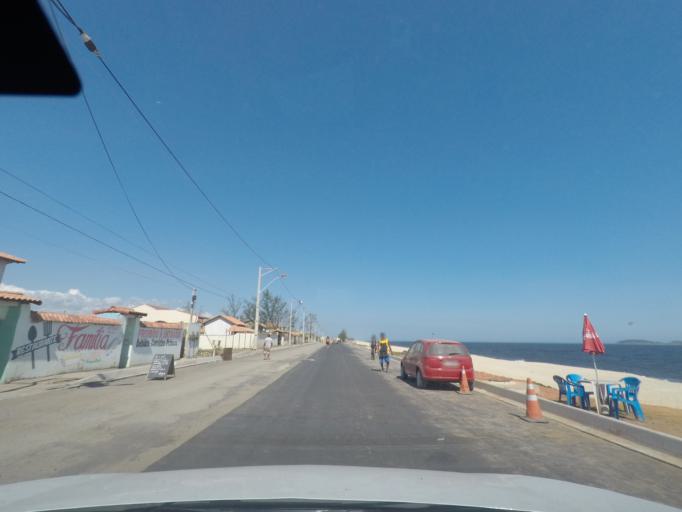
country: BR
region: Rio de Janeiro
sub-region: Marica
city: Marica
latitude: -22.9704
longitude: -42.9555
